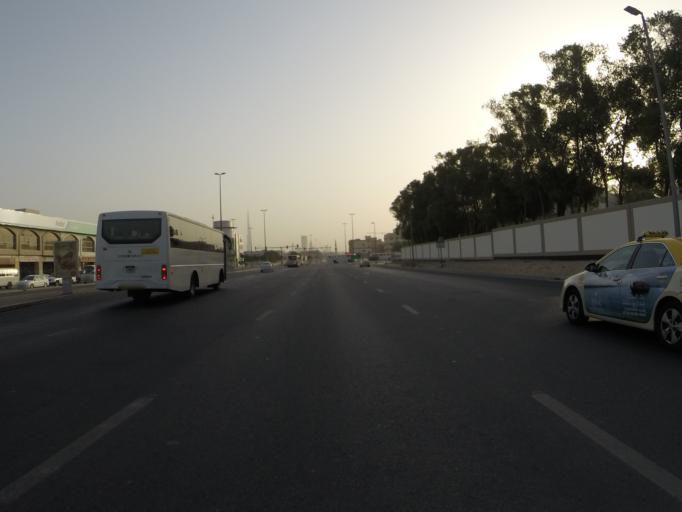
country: AE
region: Dubai
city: Dubai
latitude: 25.1466
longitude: 55.2460
